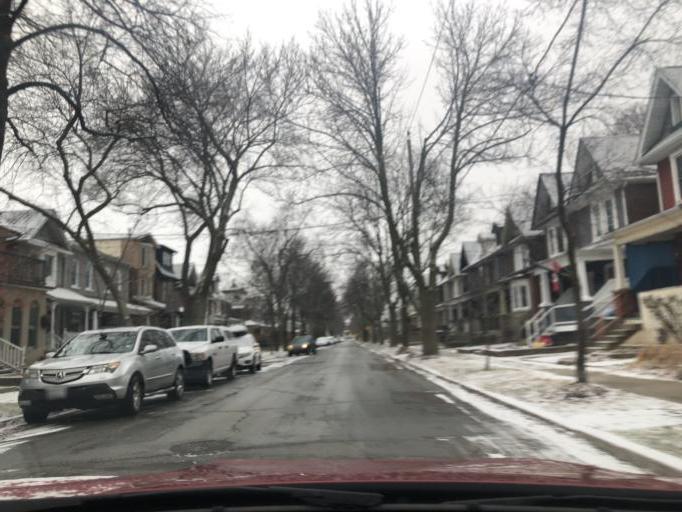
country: CA
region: Ontario
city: Toronto
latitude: 43.6837
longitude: -79.3420
